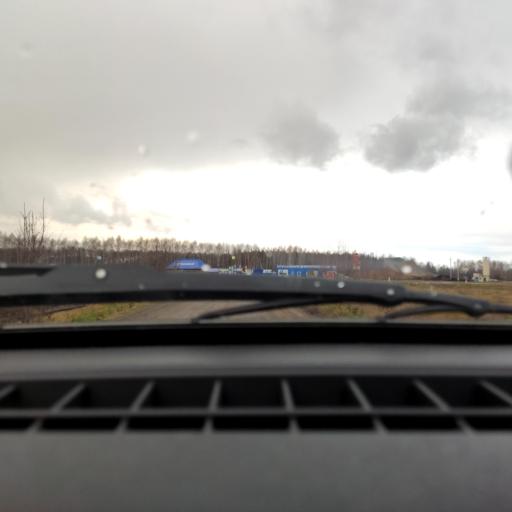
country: RU
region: Bashkortostan
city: Iglino
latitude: 54.7446
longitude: 56.3149
